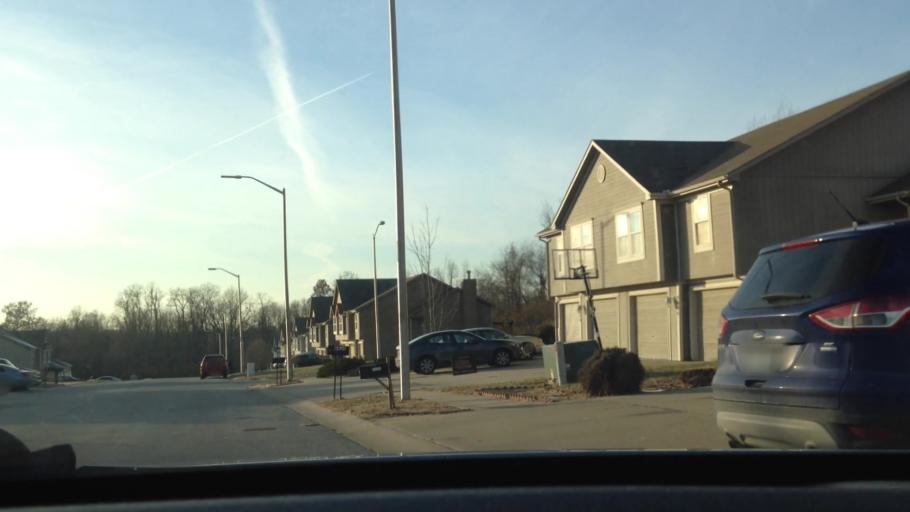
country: US
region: Missouri
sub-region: Clay County
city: Claycomo
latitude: 39.1739
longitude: -94.5044
